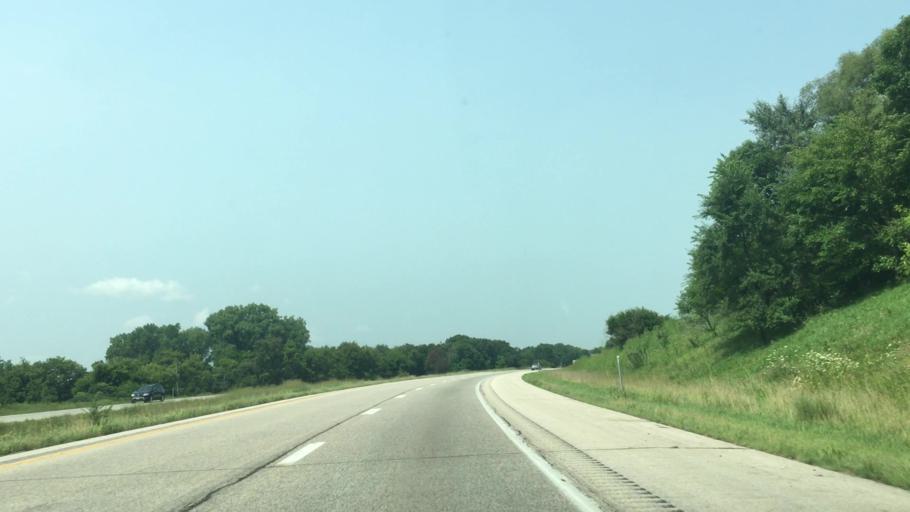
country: US
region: Iowa
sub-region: Linn County
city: Center Point
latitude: 42.1318
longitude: -91.7285
